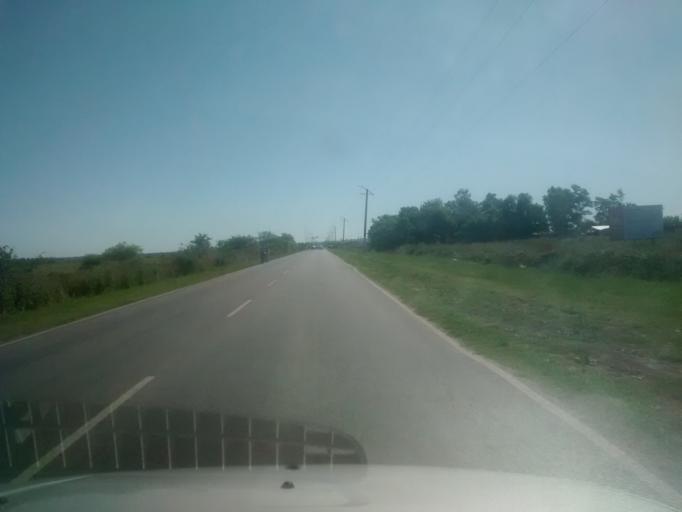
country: AR
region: Buenos Aires
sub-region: Partido de Berisso
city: Berisso
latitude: -34.8898
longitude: -57.8685
